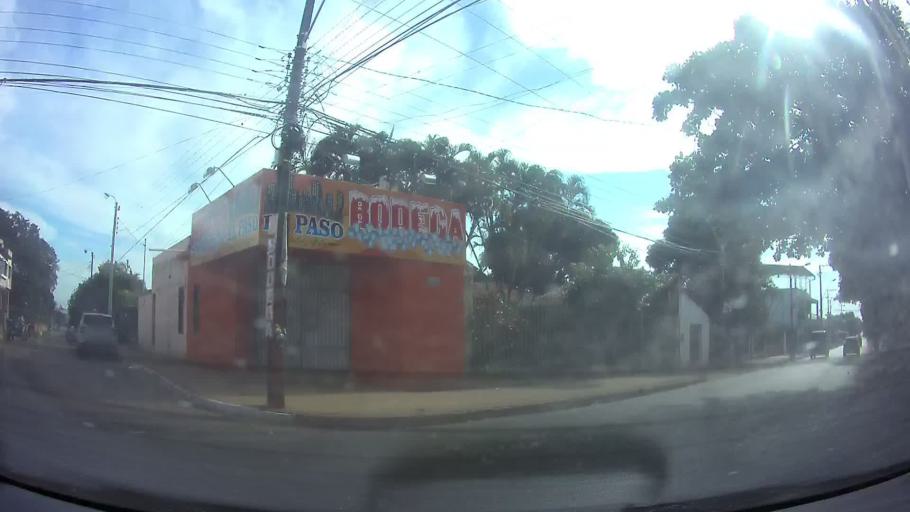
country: PY
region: Central
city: Fernando de la Mora
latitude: -25.3296
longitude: -57.5630
